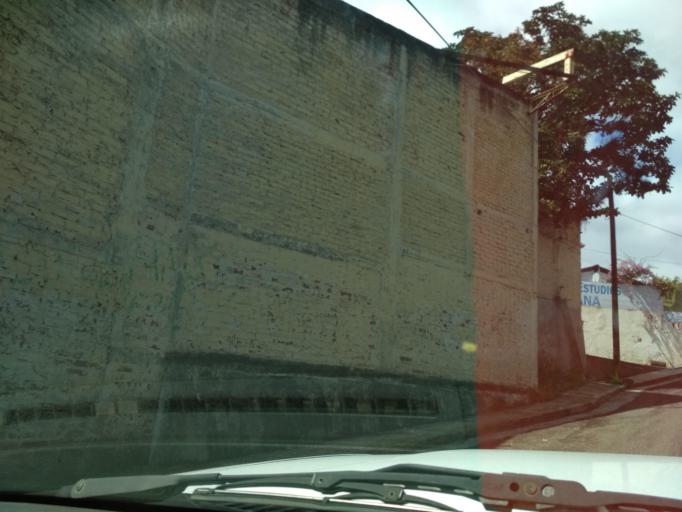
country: MX
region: Veracruz
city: Coatepec
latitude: 19.4529
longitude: -96.9372
